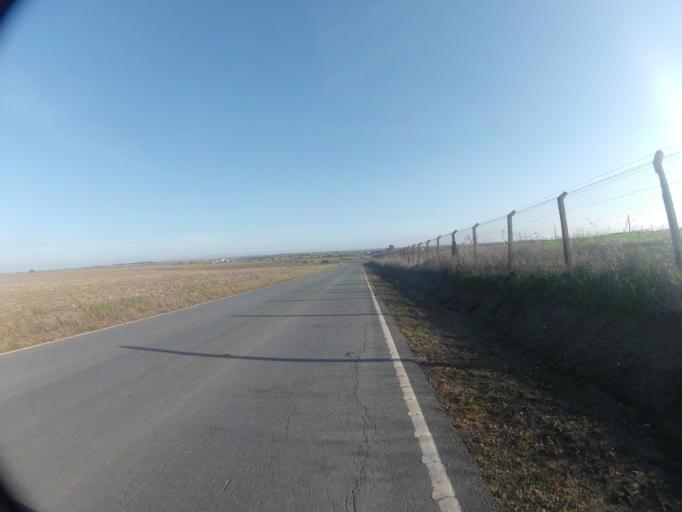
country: ES
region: Andalusia
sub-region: Provincia de Huelva
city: Huelva
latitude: 37.3112
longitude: -6.9172
